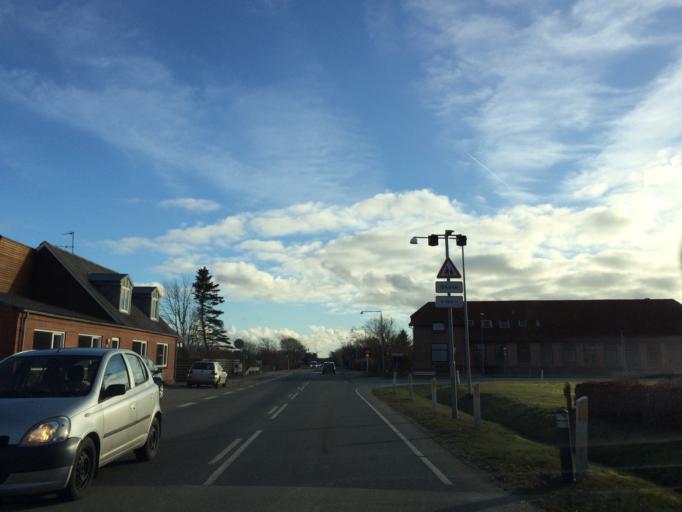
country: DK
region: Central Jutland
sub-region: Lemvig Kommune
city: Lemvig
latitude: 56.4205
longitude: 8.3064
